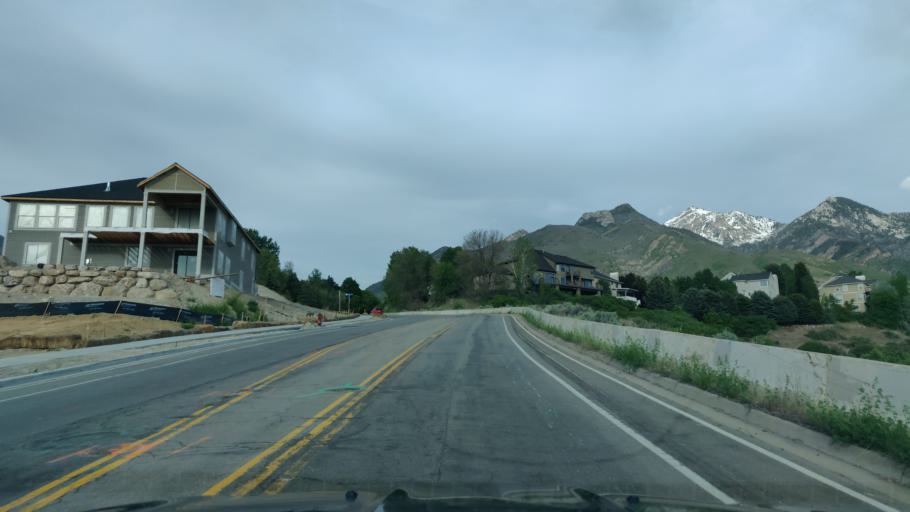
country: US
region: Utah
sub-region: Salt Lake County
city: Little Cottonwood Creek Valley
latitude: 40.6037
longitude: -111.8148
